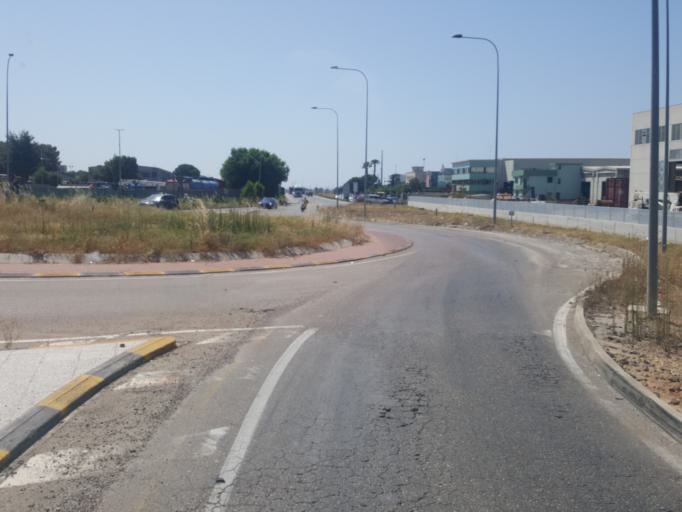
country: IT
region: Apulia
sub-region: Provincia di Taranto
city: Massafra
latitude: 40.5620
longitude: 17.1322
